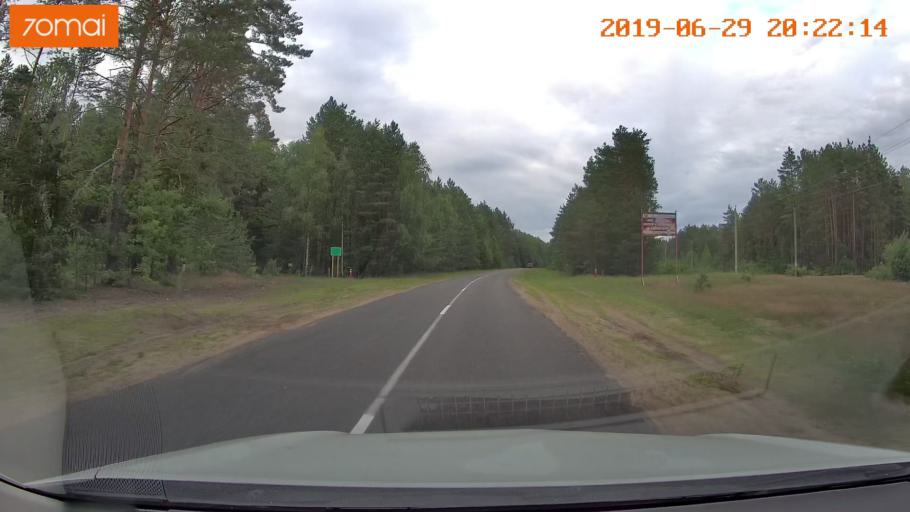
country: BY
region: Brest
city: Asnyezhytsy
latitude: 52.4294
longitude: 26.2537
